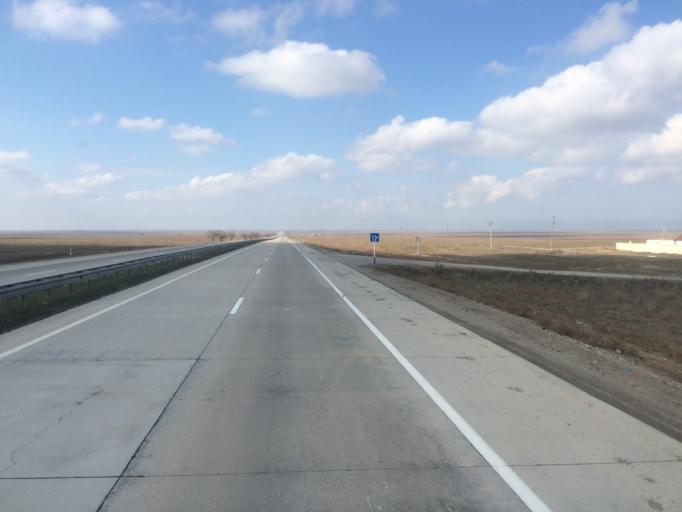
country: KZ
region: Ongtustik Qazaqstan
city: Temirlanovka
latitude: 42.8287
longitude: 69.1322
